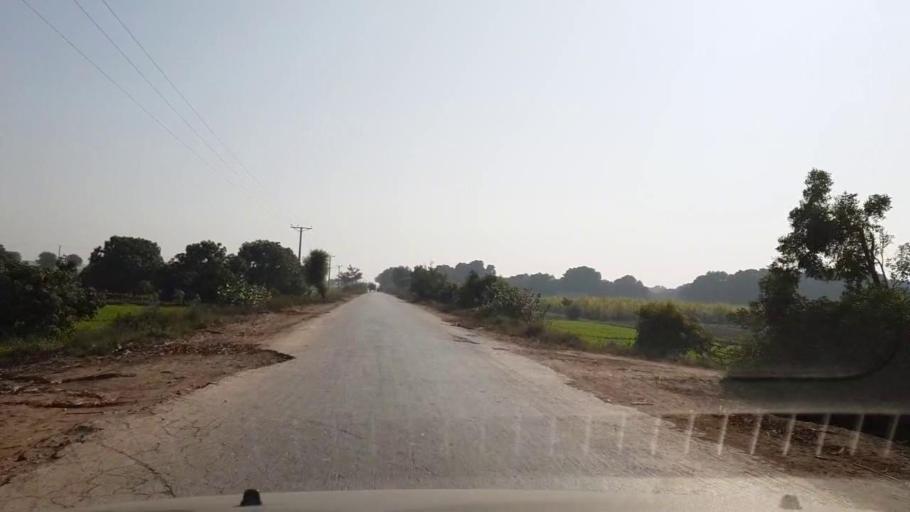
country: PK
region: Sindh
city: Tando Jam
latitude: 25.5241
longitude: 68.5920
